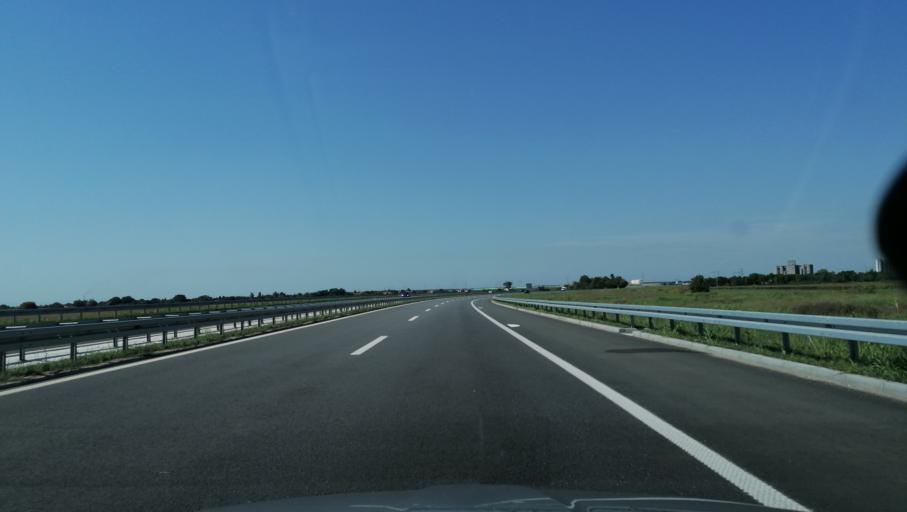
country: RS
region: Central Serbia
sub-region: Belgrade
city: Surcin
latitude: 44.7711
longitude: 20.2634
